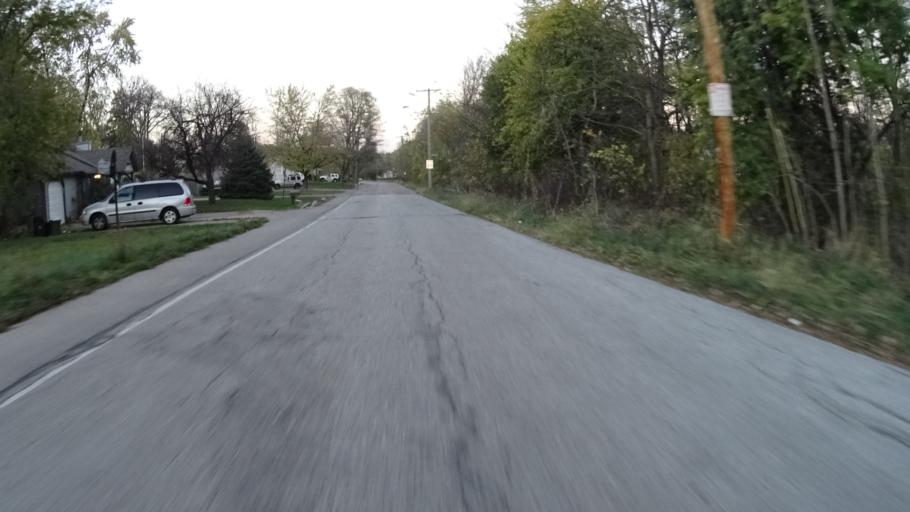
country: US
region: Nebraska
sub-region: Sarpy County
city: Offutt Air Force Base
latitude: 41.1840
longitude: -95.9530
